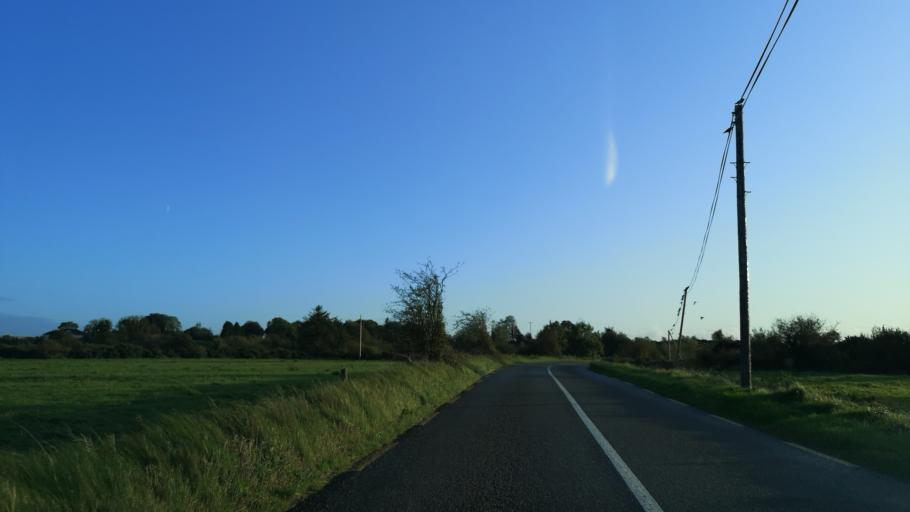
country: IE
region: Connaught
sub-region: Roscommon
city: Castlerea
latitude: 53.7037
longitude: -8.5661
